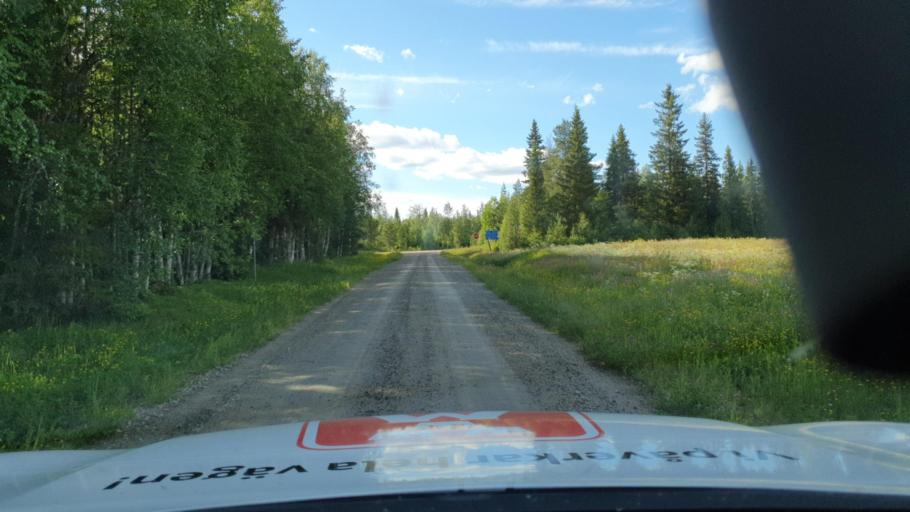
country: SE
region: Vaesterbotten
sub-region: Lycksele Kommun
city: Soderfors
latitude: 64.4852
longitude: 18.2787
